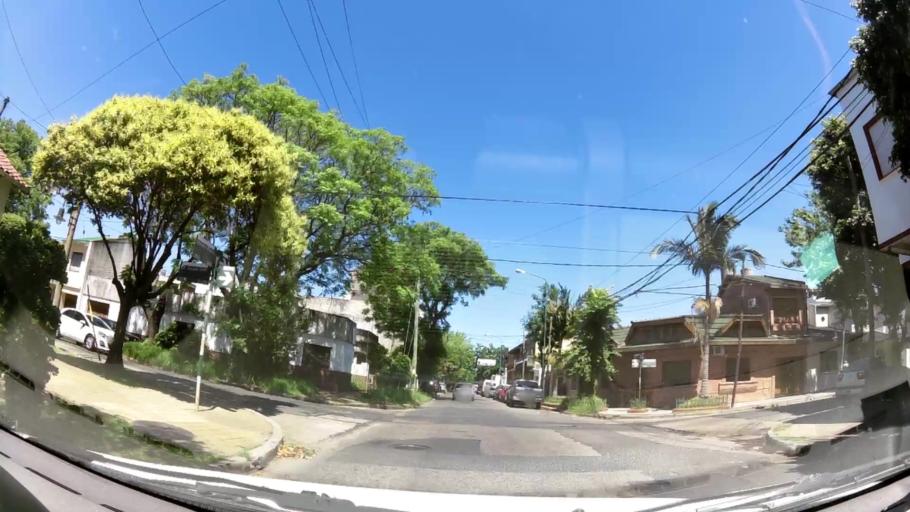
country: AR
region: Buenos Aires
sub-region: Partido de Vicente Lopez
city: Olivos
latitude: -34.5129
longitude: -58.5025
